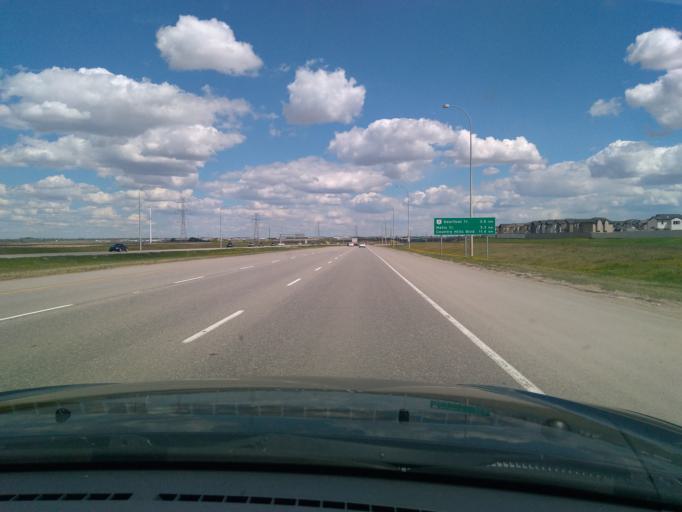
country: CA
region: Alberta
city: Calgary
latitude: 51.1738
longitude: -114.0539
